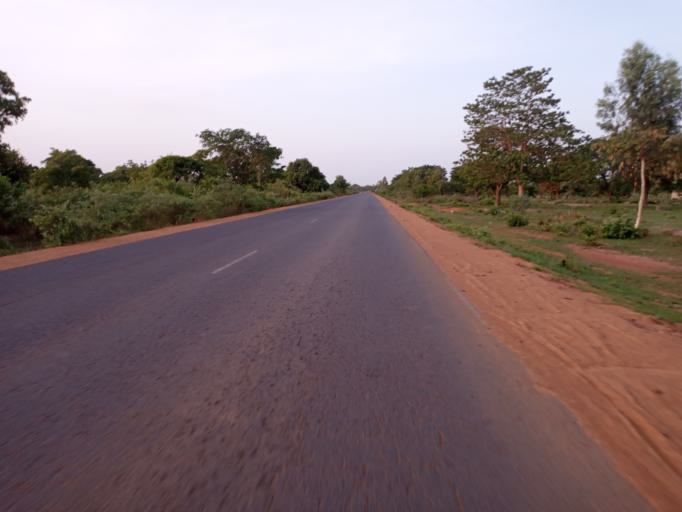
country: ML
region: Bamako
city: Bamako
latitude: 12.2916
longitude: -8.1682
